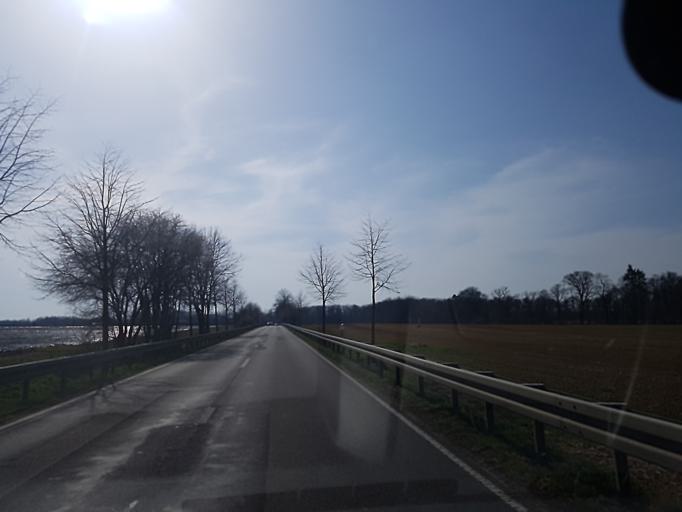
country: DE
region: Brandenburg
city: Calau
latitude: 51.7593
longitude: 13.9982
